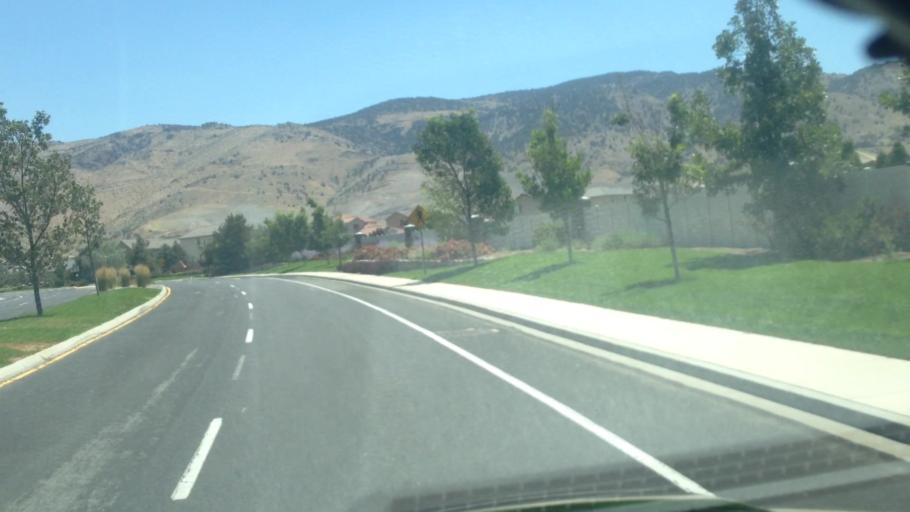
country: US
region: Nevada
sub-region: Washoe County
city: Sparks
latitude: 39.4148
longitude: -119.7283
